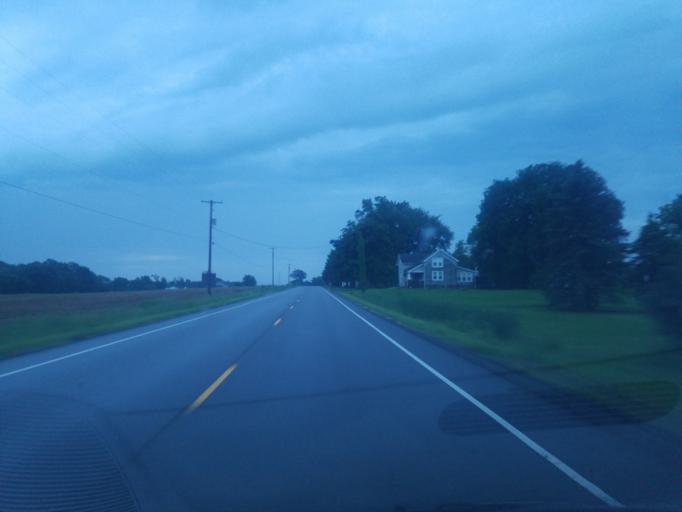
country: US
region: Ohio
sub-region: Mahoning County
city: Canfield
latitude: 40.9861
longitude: -80.7585
